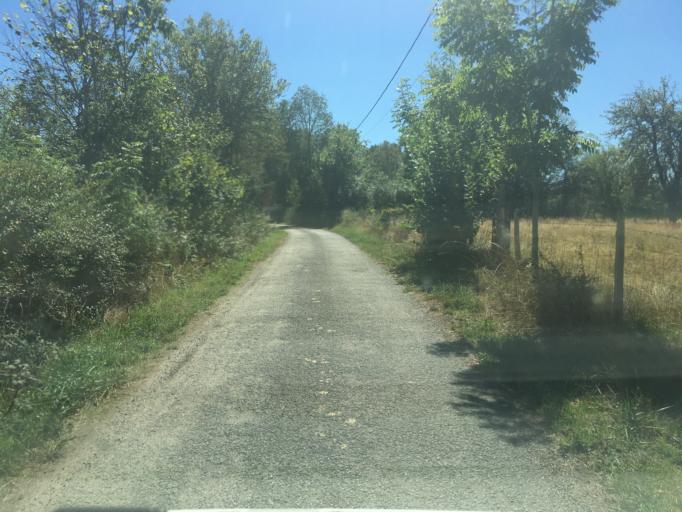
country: FR
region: Limousin
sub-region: Departement de la Correze
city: Bort-les-Orgues
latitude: 45.4370
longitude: 2.4863
